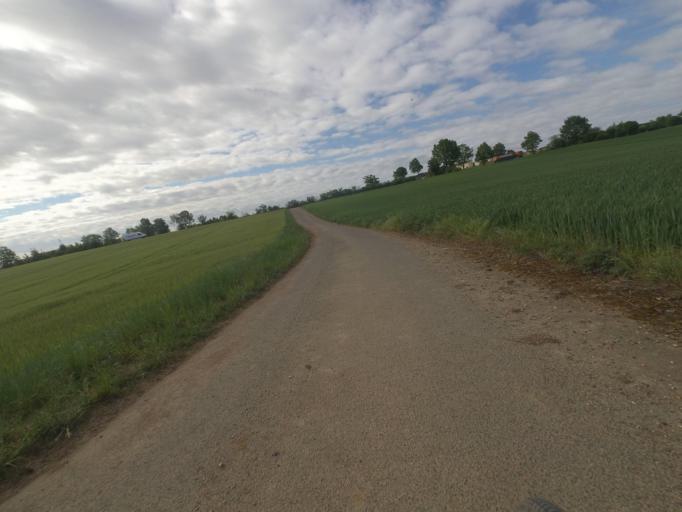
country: DE
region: Rheinland-Pfalz
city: Kirchheimbolanden
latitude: 49.6768
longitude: 8.0073
